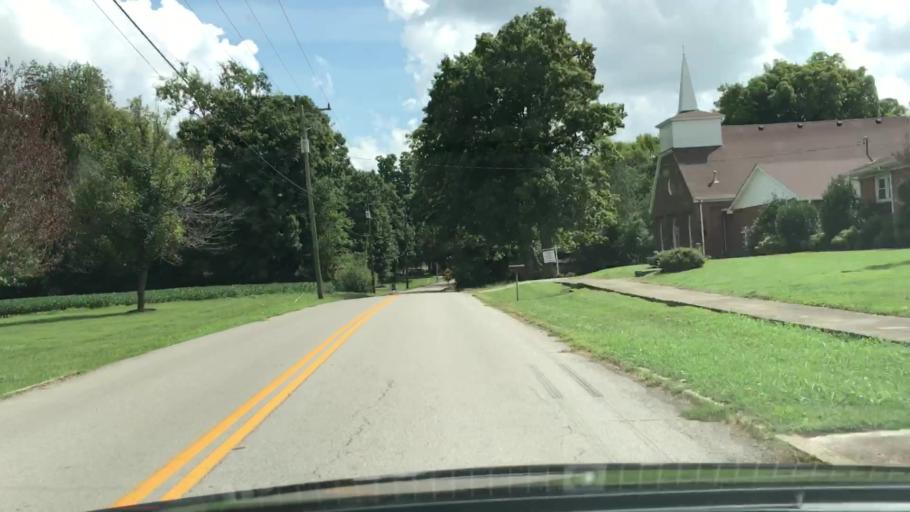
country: US
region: Kentucky
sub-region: Todd County
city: Guthrie
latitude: 36.7180
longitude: -87.0703
